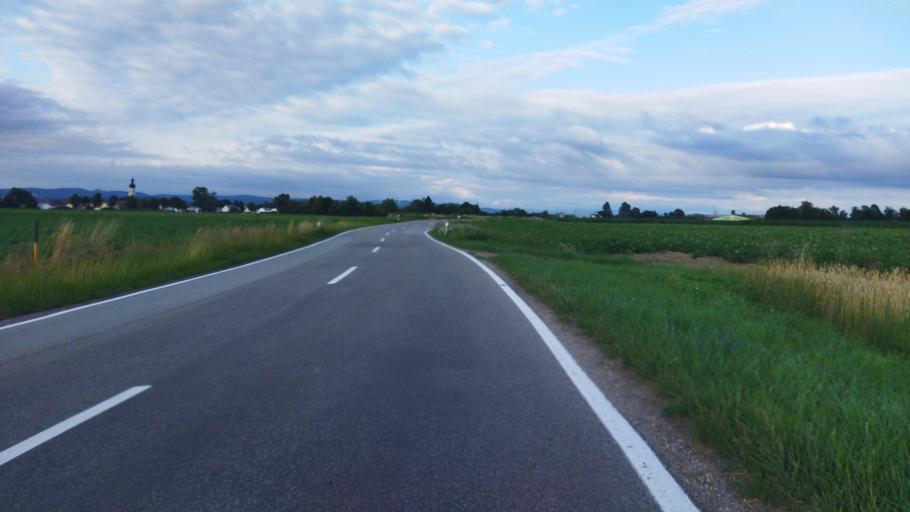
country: DE
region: Bavaria
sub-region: Upper Palatinate
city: Riekofen
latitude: 48.9645
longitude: 12.3181
